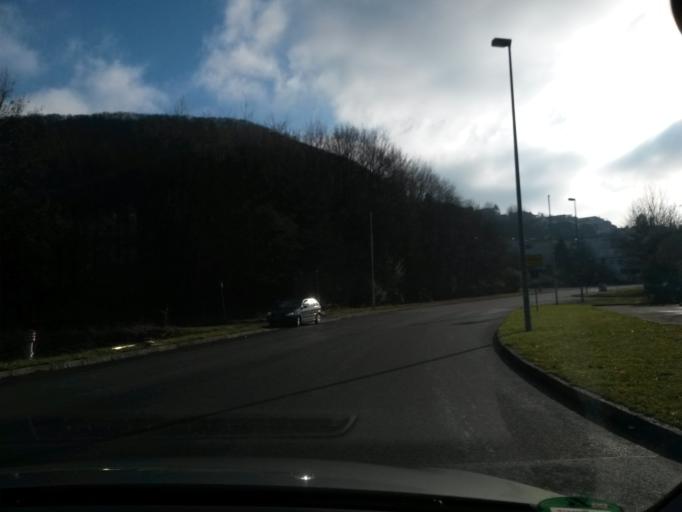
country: DE
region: Baden-Wuerttemberg
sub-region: Regierungsbezirk Stuttgart
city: Bad Uberkingen
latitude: 48.6065
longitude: 9.8017
